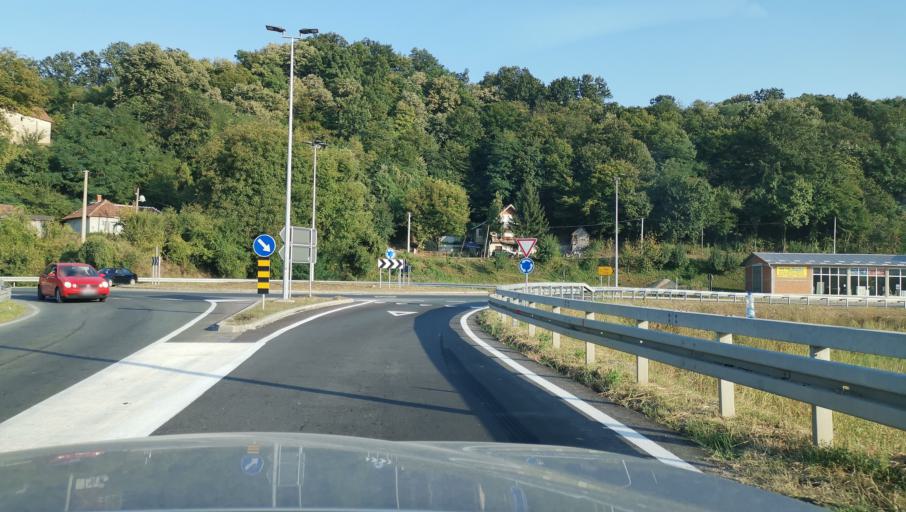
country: RS
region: Central Serbia
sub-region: Kolubarski Okrug
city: Ljig
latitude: 44.2287
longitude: 20.2474
